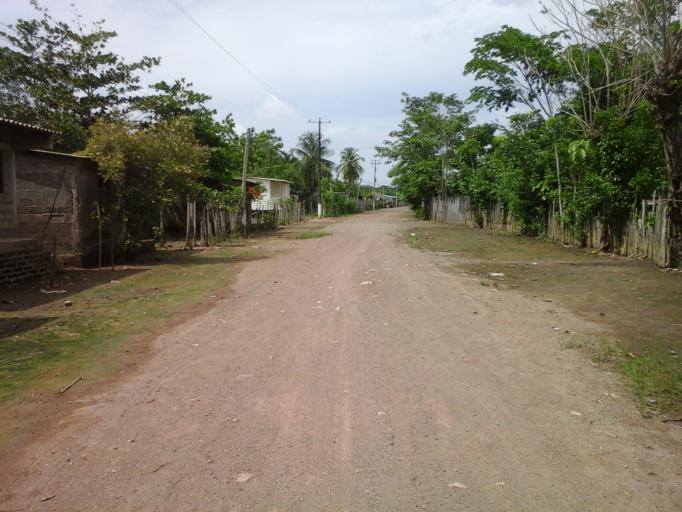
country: CO
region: Cordoba
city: Lorica
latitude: 9.1349
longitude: -75.8403
